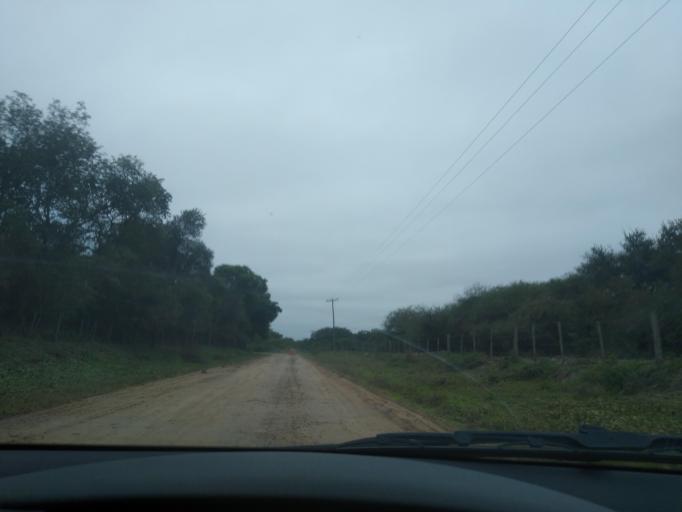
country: AR
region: Chaco
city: Colonia Benitez
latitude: -27.3487
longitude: -58.9716
